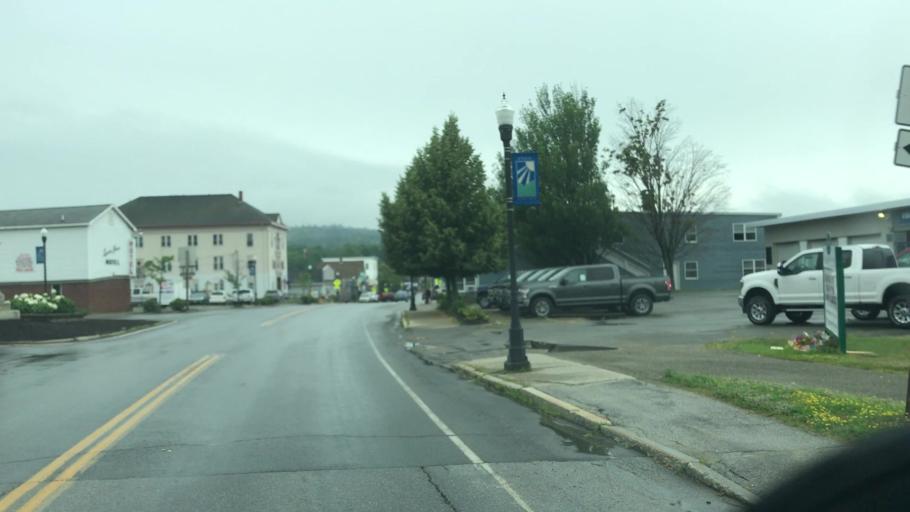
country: US
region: Maine
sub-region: Penobscot County
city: Lincoln
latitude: 45.3655
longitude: -68.5033
